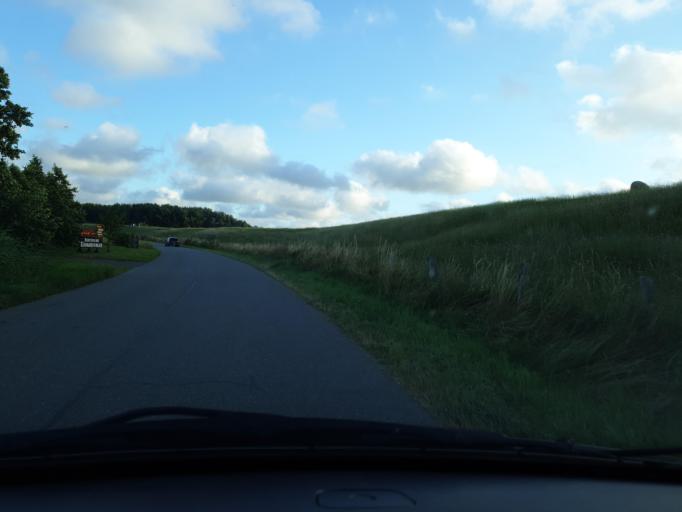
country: DE
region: Schleswig-Holstein
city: Elpersbuttel
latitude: 54.0720
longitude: 9.0145
